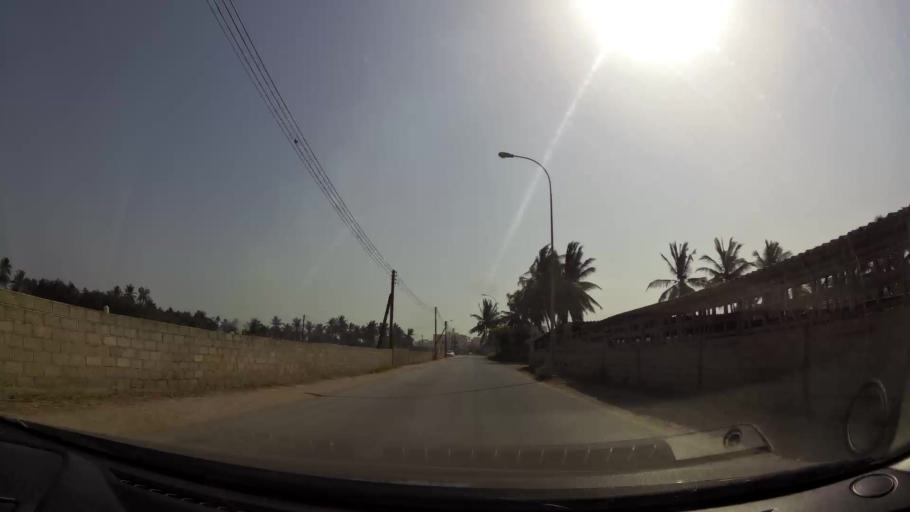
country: OM
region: Zufar
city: Salalah
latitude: 17.0034
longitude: 54.0545
